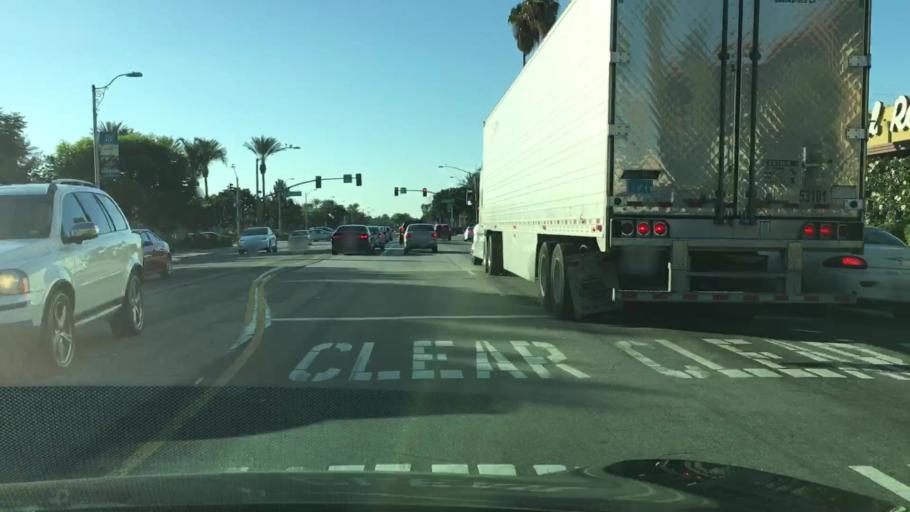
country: US
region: California
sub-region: Los Angeles County
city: Pico Rivera
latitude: 33.9827
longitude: -118.0961
